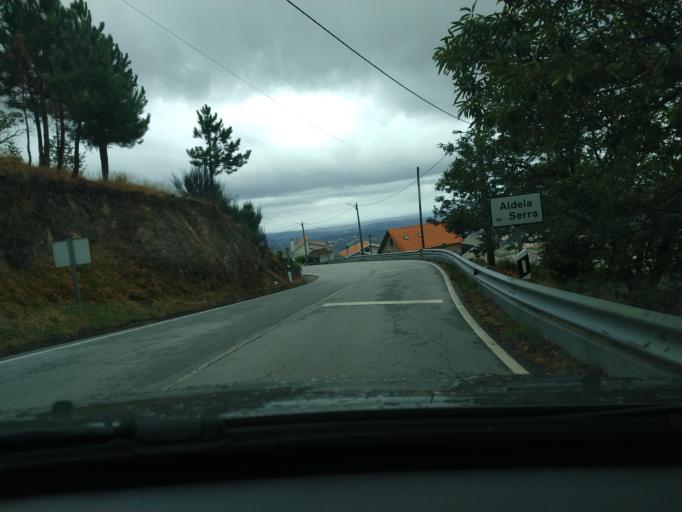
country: PT
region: Guarda
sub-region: Seia
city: Seia
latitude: 40.4183
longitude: -7.6828
